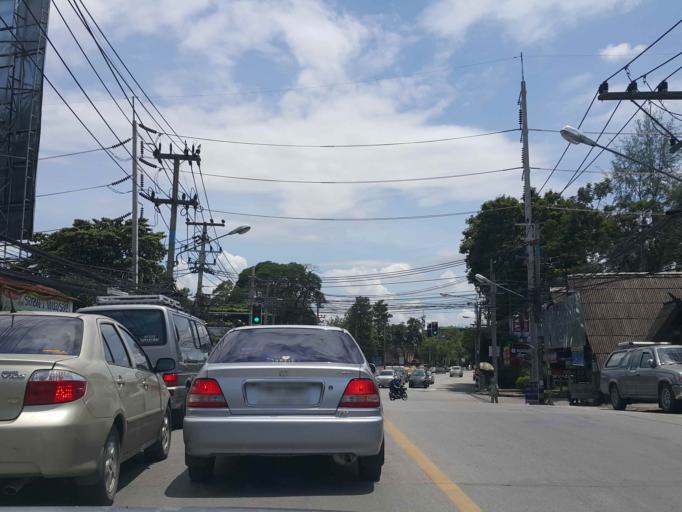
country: TH
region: Chiang Mai
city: Chiang Mai
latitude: 18.7742
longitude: 98.9807
